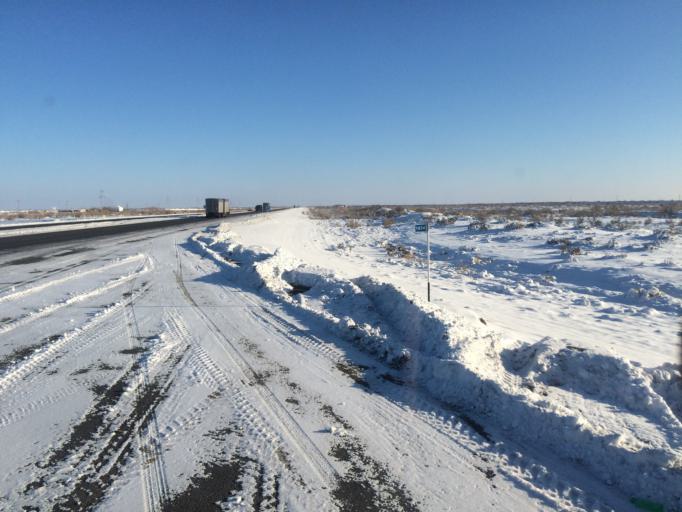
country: KZ
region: Qyzylorda
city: Belkol
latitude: 44.7731
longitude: 65.7640
